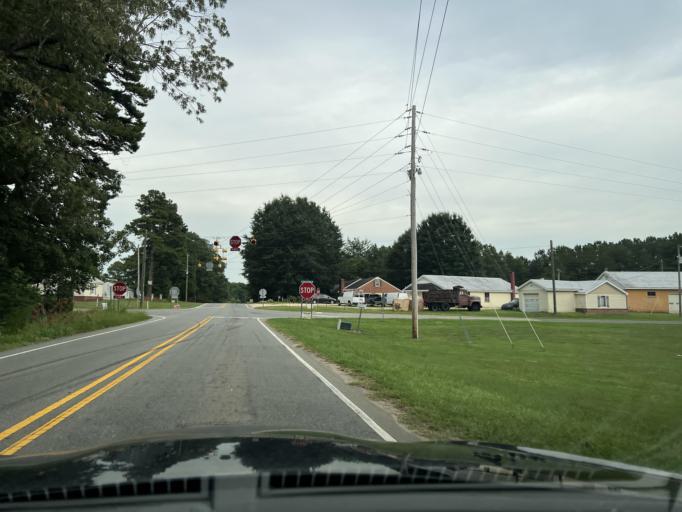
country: US
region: North Carolina
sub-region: Wake County
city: Wake Forest
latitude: 36.0139
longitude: -78.5657
